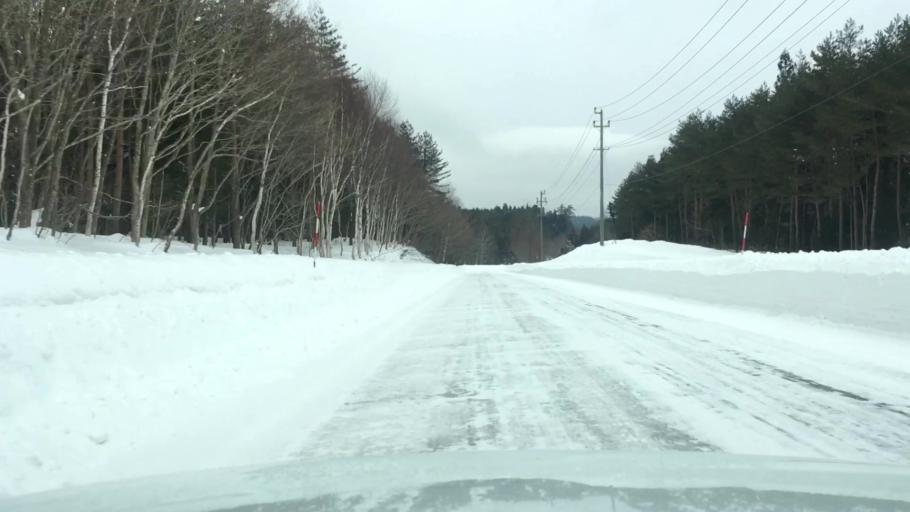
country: JP
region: Akita
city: Hanawa
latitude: 39.9877
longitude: 140.9991
